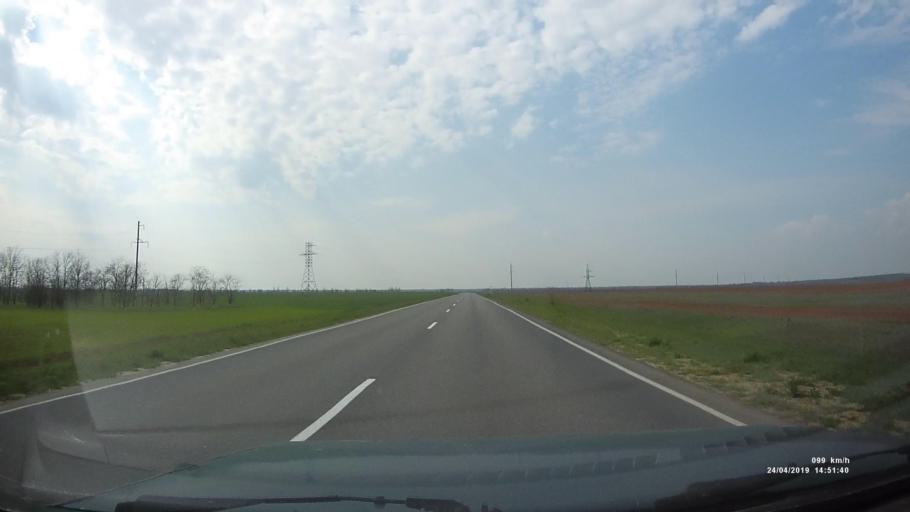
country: RU
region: Rostov
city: Remontnoye
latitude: 46.5266
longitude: 43.6962
